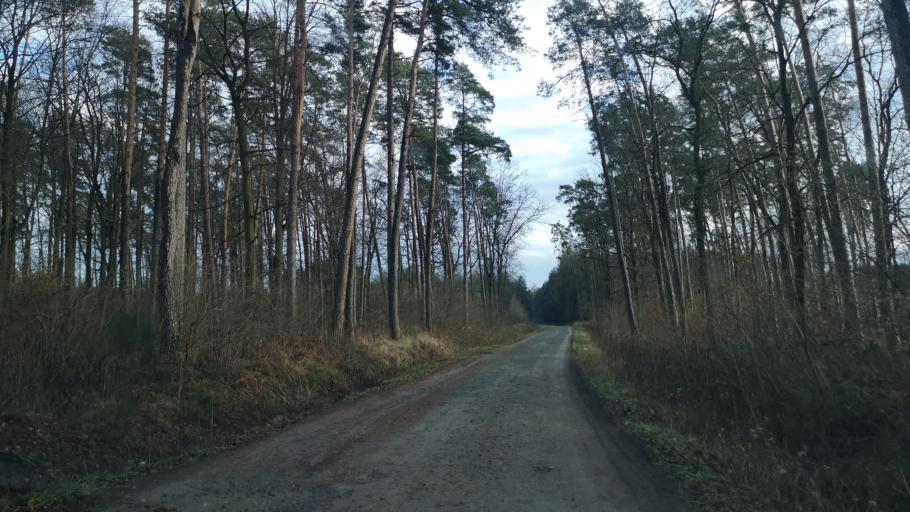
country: PL
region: Subcarpathian Voivodeship
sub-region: Powiat lezajski
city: Piskorowice
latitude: 50.2554
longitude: 22.5601
